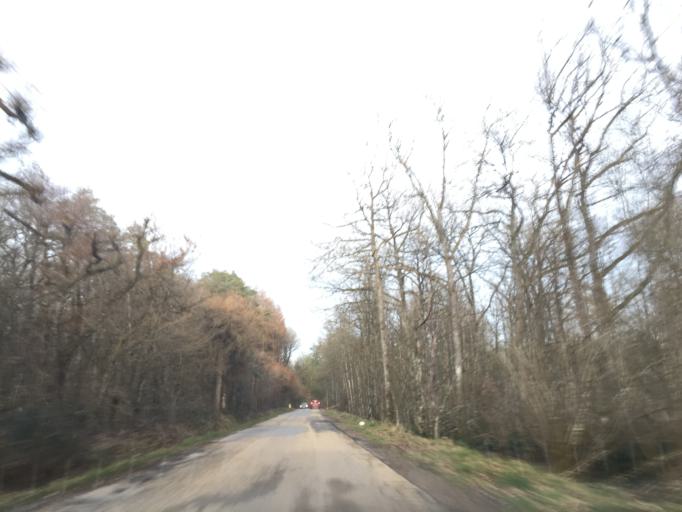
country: BE
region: Wallonia
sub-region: Province du Luxembourg
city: Durbuy
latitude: 50.3222
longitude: 5.4843
